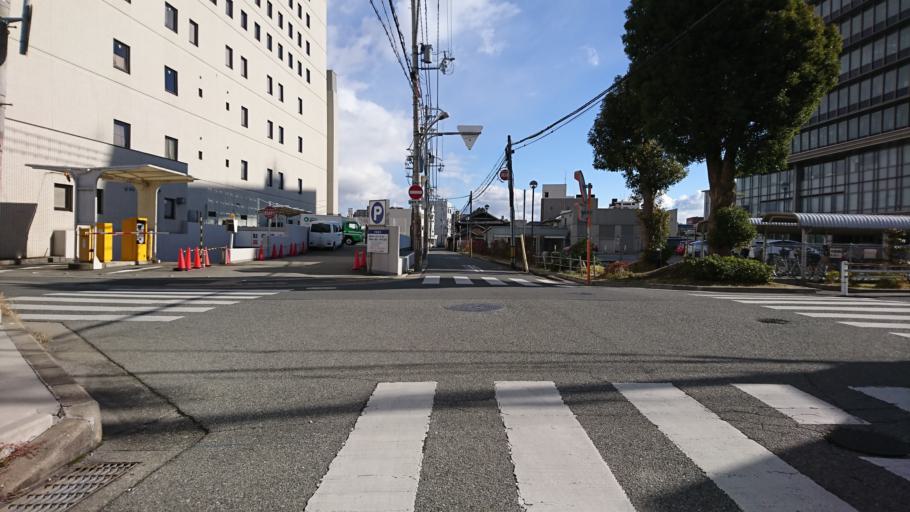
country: JP
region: Hyogo
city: Kakogawacho-honmachi
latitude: 34.7645
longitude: 134.8391
